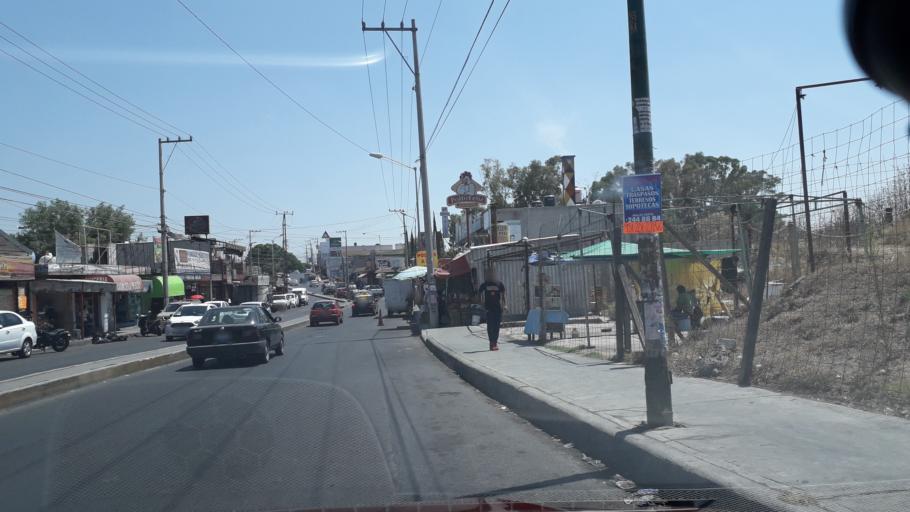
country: MX
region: Puebla
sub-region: Puebla
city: El Capulo (La Quebradora)
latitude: 18.9756
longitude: -98.2188
